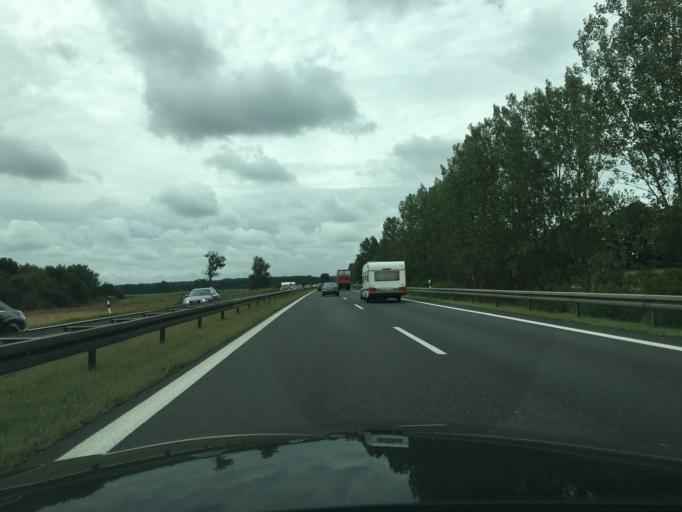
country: DE
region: Brandenburg
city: Brieselang
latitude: 52.6466
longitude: 12.9972
